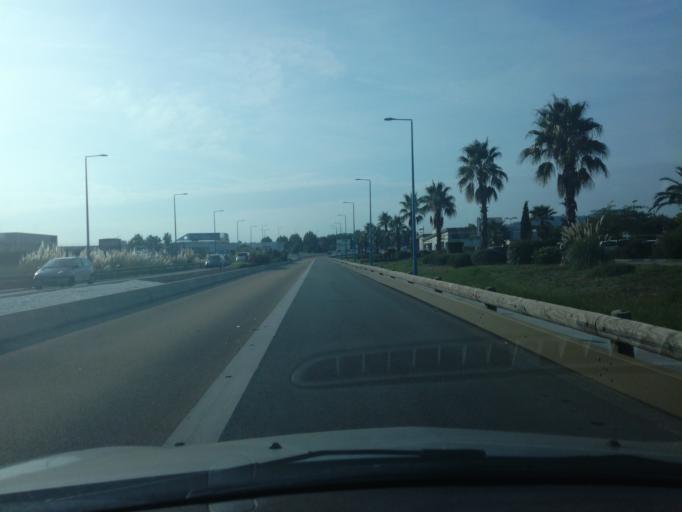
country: FR
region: Provence-Alpes-Cote d'Azur
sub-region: Departement des Alpes-Maritimes
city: Mandelieu-la-Napoule
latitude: 43.5538
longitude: 6.9469
